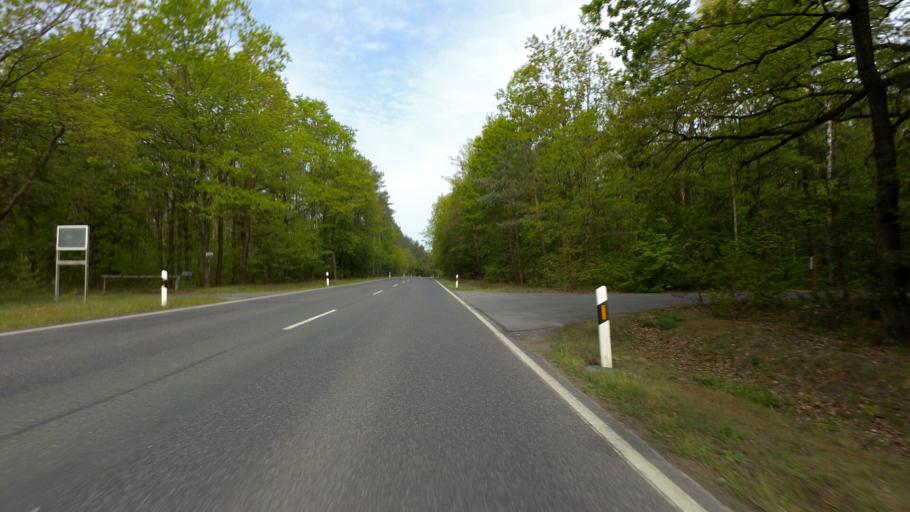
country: DE
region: Saxony
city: Laussnitz
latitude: 51.2638
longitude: 13.8557
